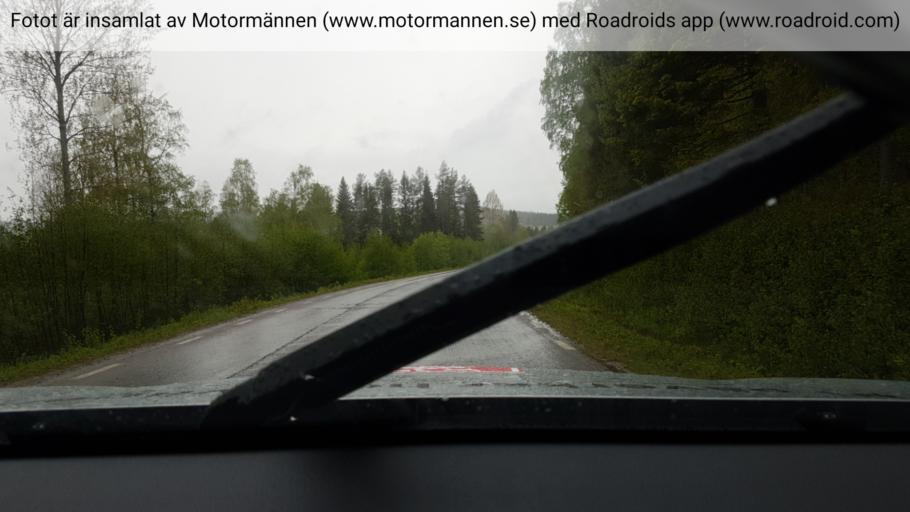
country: SE
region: Vaesterbotten
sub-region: Vannas Kommun
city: Vaennaes
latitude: 63.8677
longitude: 19.6630
